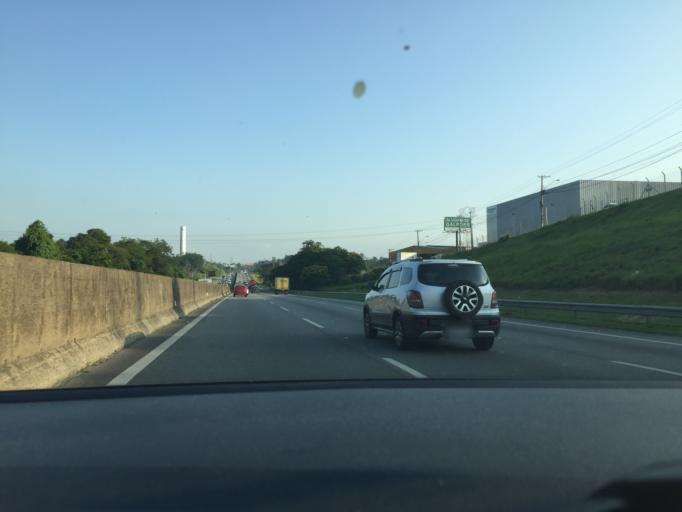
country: BR
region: Sao Paulo
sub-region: Louveira
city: Louveira
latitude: -23.1023
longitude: -46.9650
